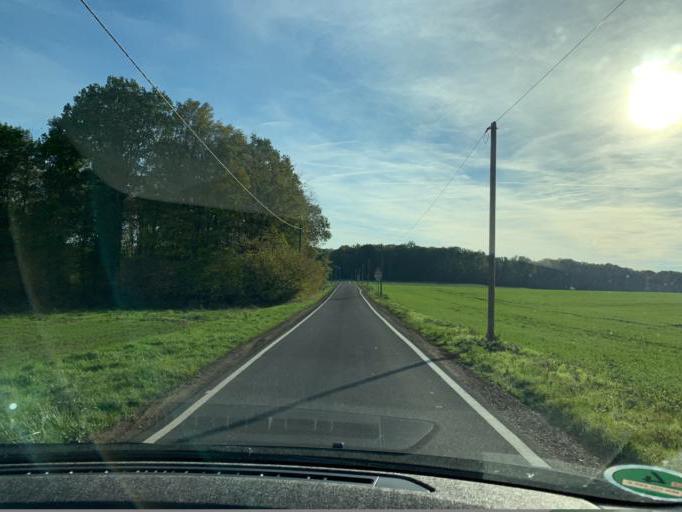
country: DE
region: North Rhine-Westphalia
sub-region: Regierungsbezirk Koln
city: Nideggen
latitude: 50.6662
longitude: 6.5086
